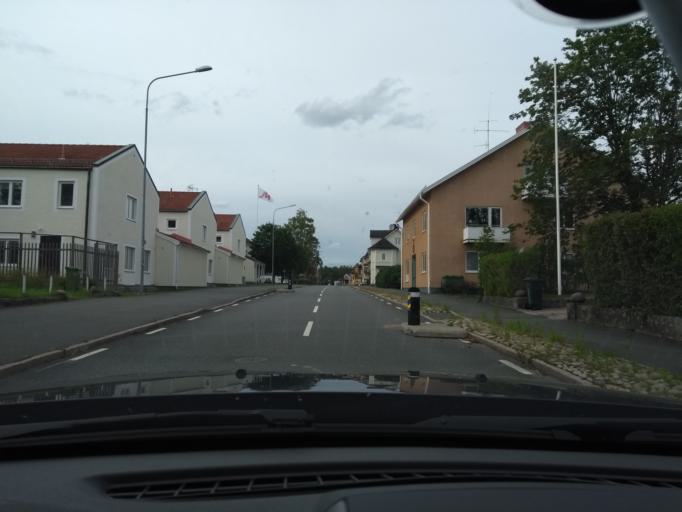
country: SE
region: Joenkoeping
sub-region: Eksjo Kommun
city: Mariannelund
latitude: 57.6148
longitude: 15.5748
